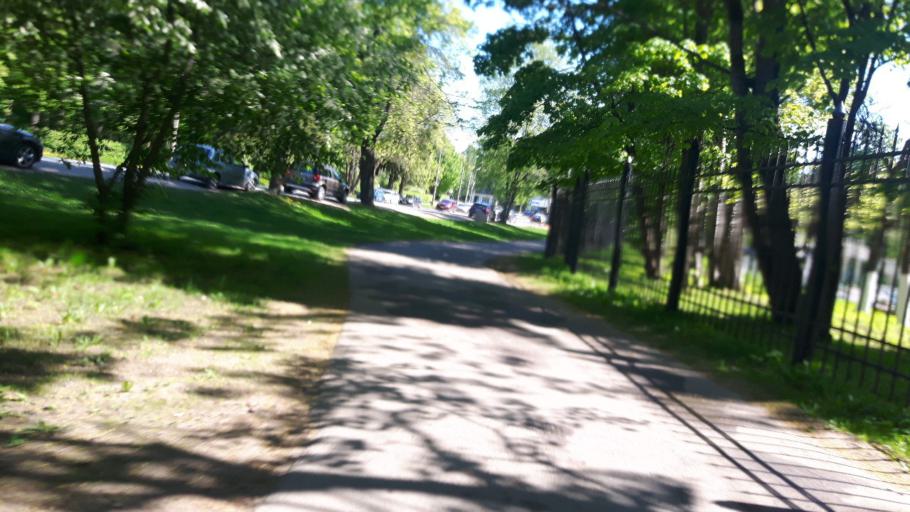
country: RU
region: St.-Petersburg
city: Zelenogorsk
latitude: 60.1920
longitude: 29.6974
